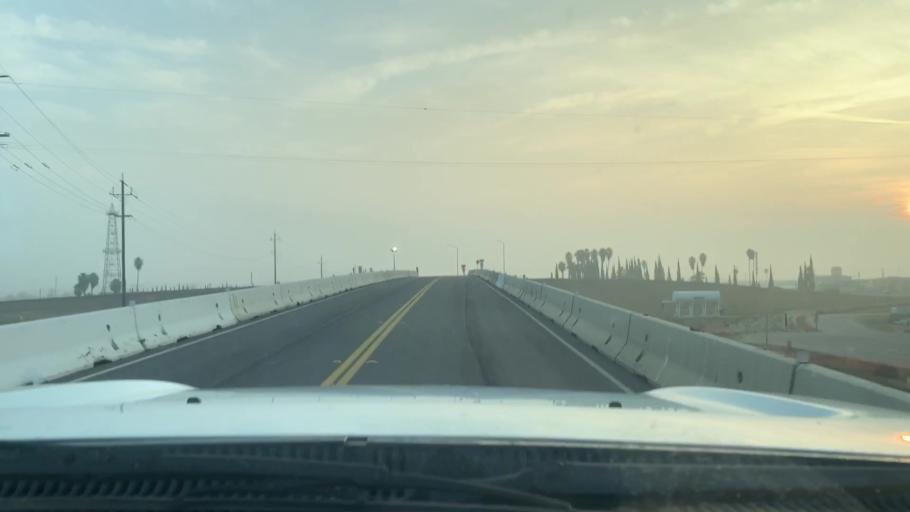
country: US
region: California
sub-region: Kern County
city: McFarland
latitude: 35.6019
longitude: -119.2142
